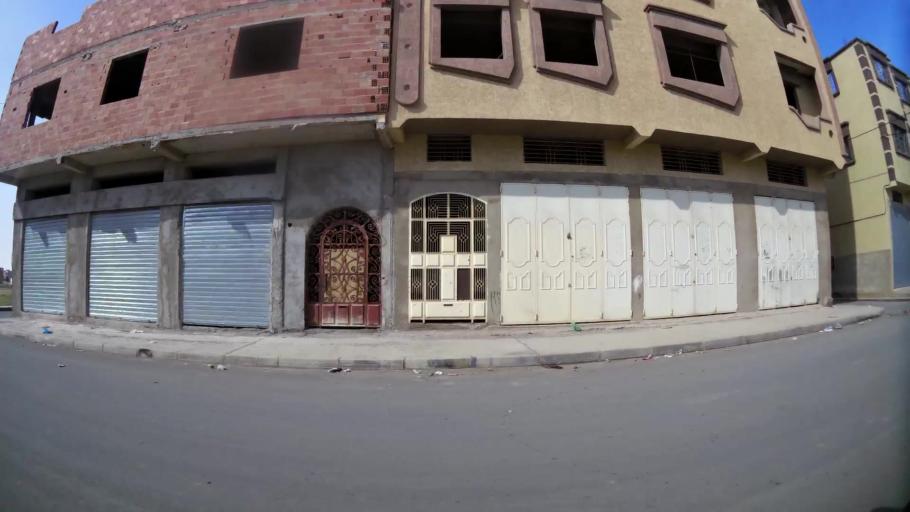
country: MA
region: Oriental
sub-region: Oujda-Angad
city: Oujda
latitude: 34.7128
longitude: -1.8839
